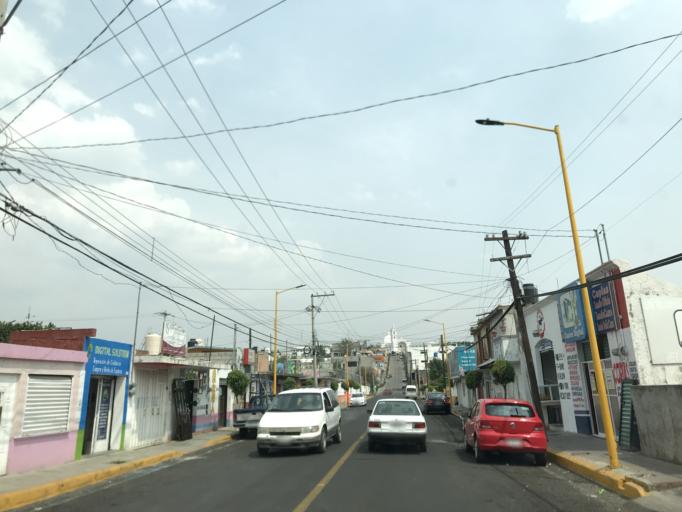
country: MX
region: Tlaxcala
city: Panotla
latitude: 19.3176
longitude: -98.2705
